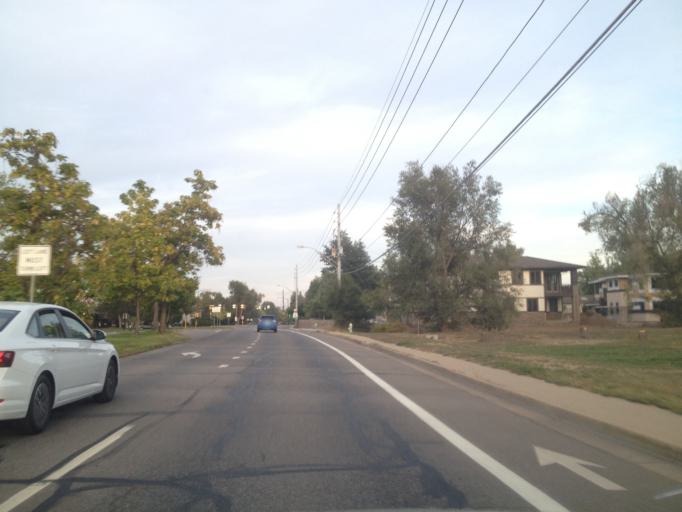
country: US
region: Colorado
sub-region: Boulder County
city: Boulder
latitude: 40.0000
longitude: -105.2278
